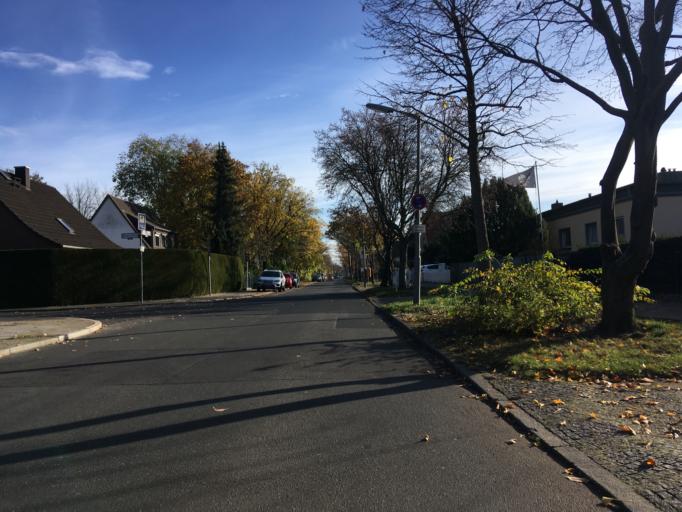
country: DE
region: Berlin
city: Rudow
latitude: 52.4337
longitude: 13.4909
